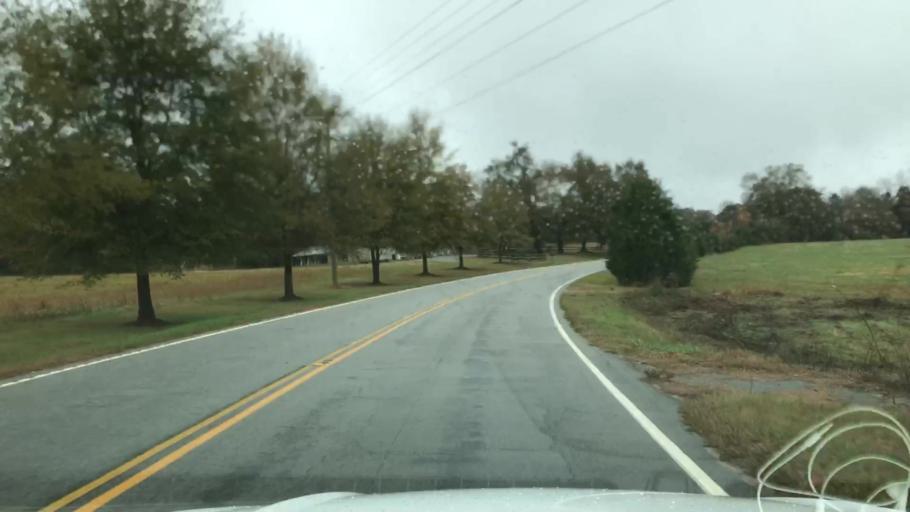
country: US
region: South Carolina
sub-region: Spartanburg County
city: Roebuck
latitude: 34.8164
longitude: -81.9270
